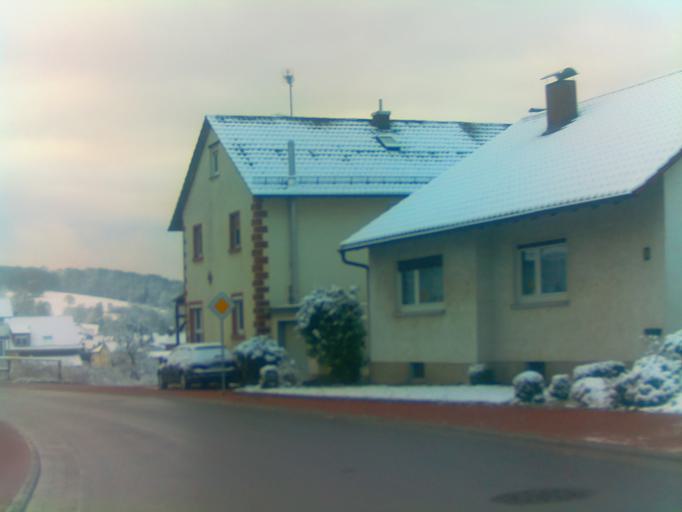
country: DE
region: Hesse
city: Unter-Abtsteinach
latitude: 49.5324
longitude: 8.7867
